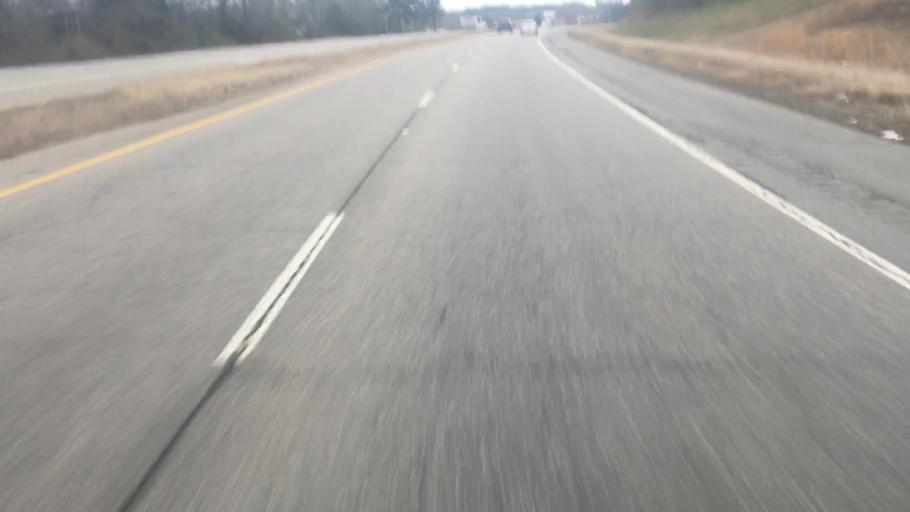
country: US
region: Alabama
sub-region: Walker County
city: Cordova
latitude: 33.8213
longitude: -87.1579
